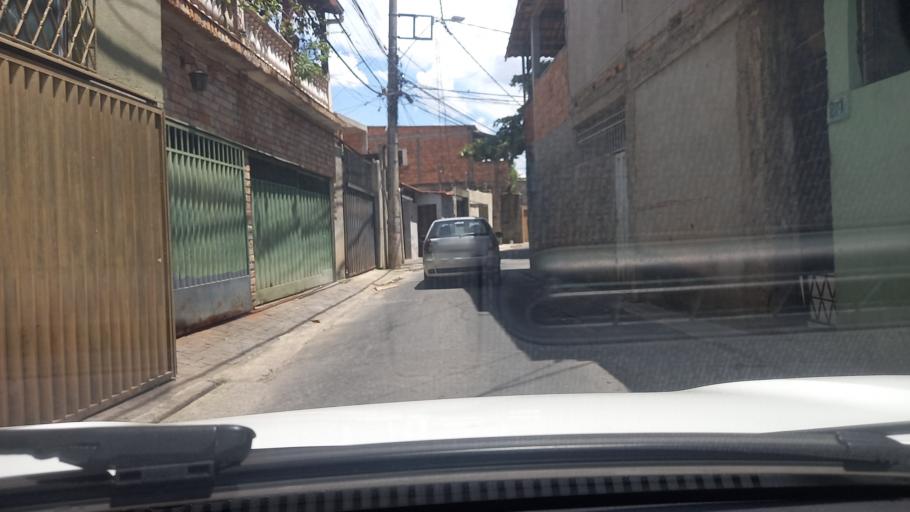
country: BR
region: Minas Gerais
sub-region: Belo Horizonte
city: Belo Horizonte
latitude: -19.9195
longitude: -43.9839
